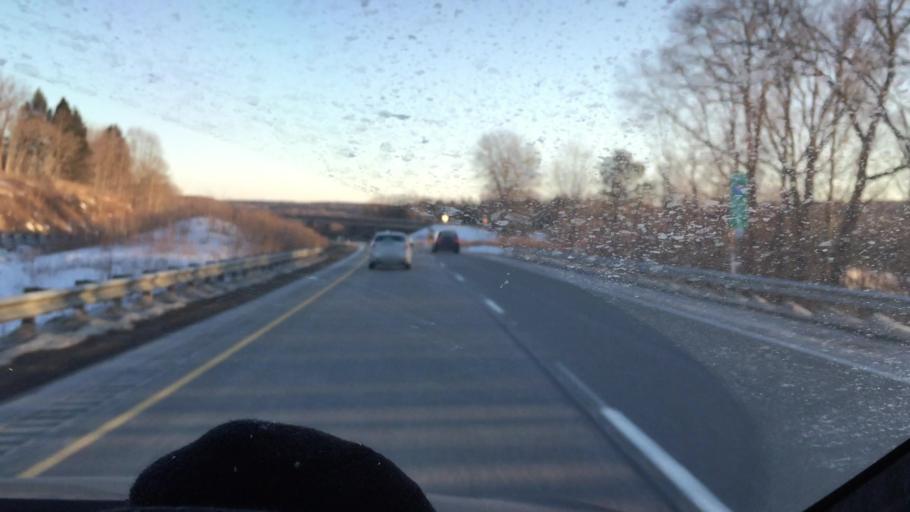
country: US
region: Pennsylvania
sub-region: Crawford County
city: Meadville
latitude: 41.6739
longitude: -80.2096
